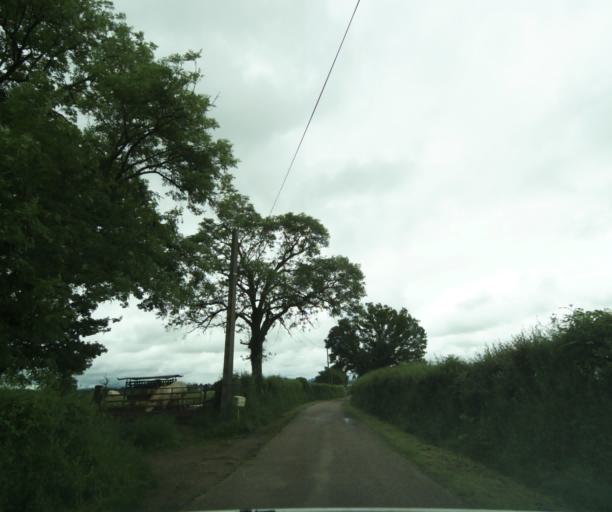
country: FR
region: Bourgogne
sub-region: Departement de Saone-et-Loire
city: Charolles
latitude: 46.4601
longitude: 4.2935
